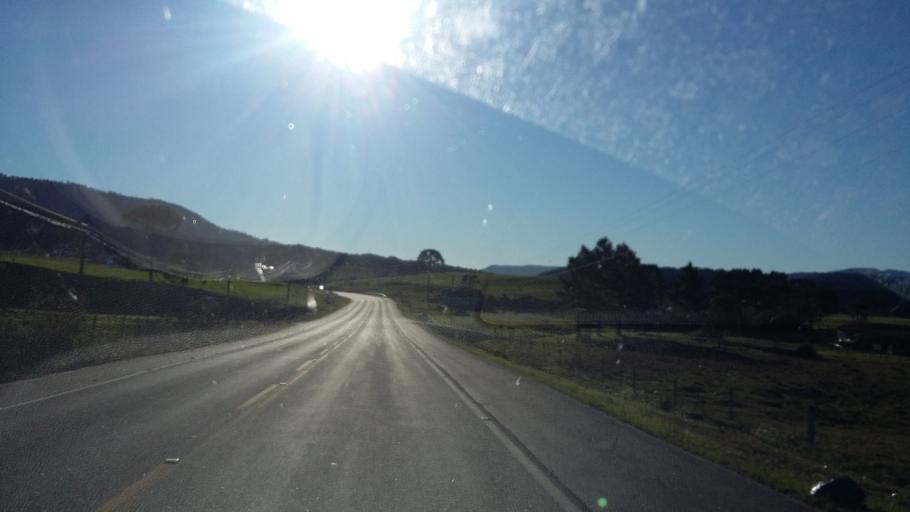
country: BR
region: Santa Catarina
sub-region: Lauro Muller
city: Lauro Muller
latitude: -28.0180
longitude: -49.5205
